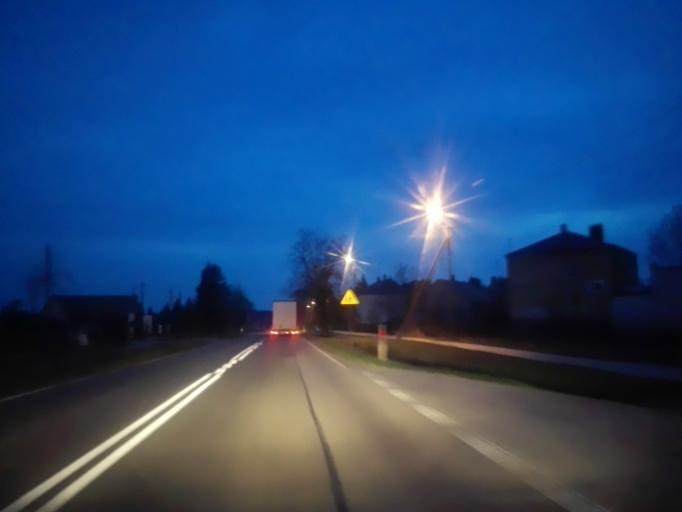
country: PL
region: Podlasie
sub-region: Powiat lomzynski
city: Sniadowo
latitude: 53.0394
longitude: 21.9854
